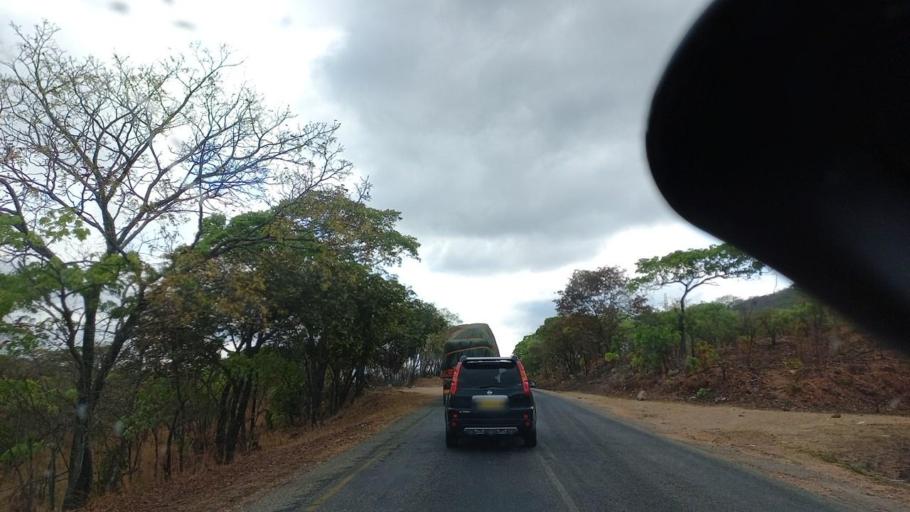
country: ZM
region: Lusaka
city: Chongwe
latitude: -15.1500
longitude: 29.3621
